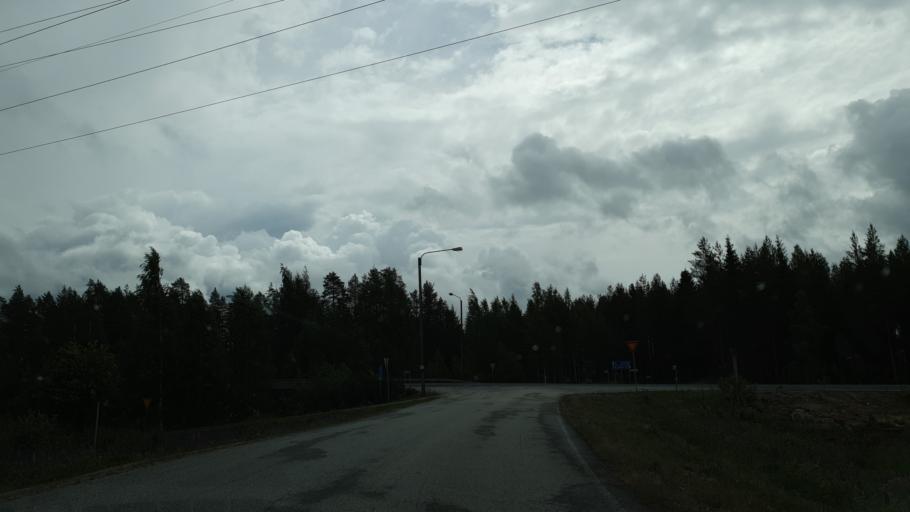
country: FI
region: Kainuu
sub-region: Kehys-Kainuu
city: Kuhmo
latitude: 64.0929
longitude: 29.4347
